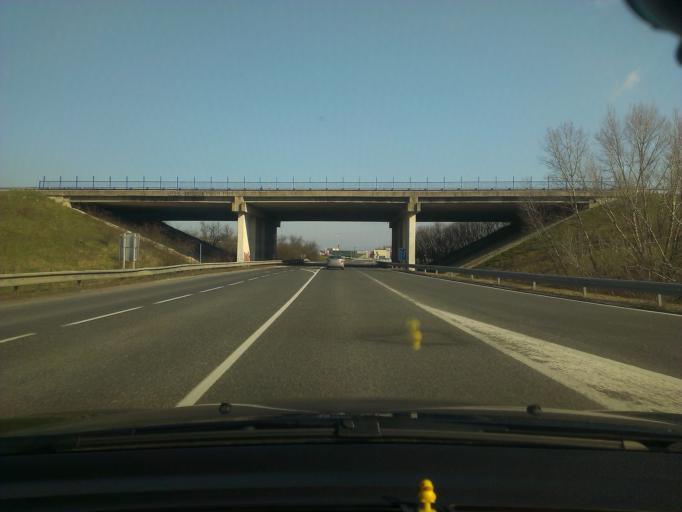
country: SK
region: Trnavsky
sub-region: Okres Trnava
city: Piestany
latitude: 48.6485
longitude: 17.8389
